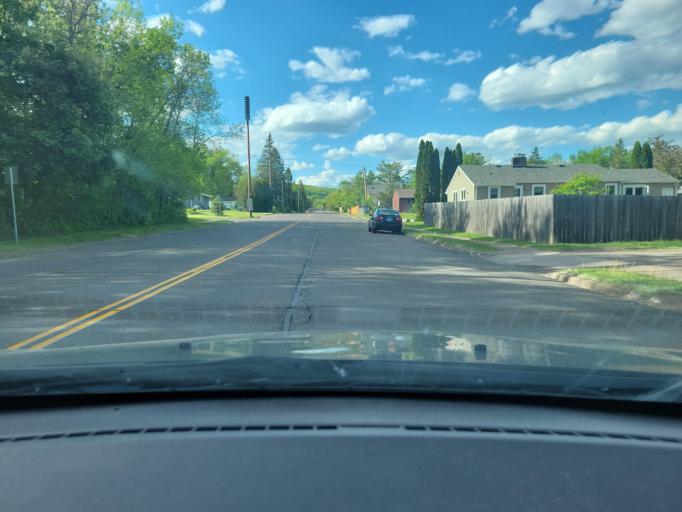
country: US
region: Minnesota
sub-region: Saint Louis County
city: Arnold
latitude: 46.8358
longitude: -92.0293
